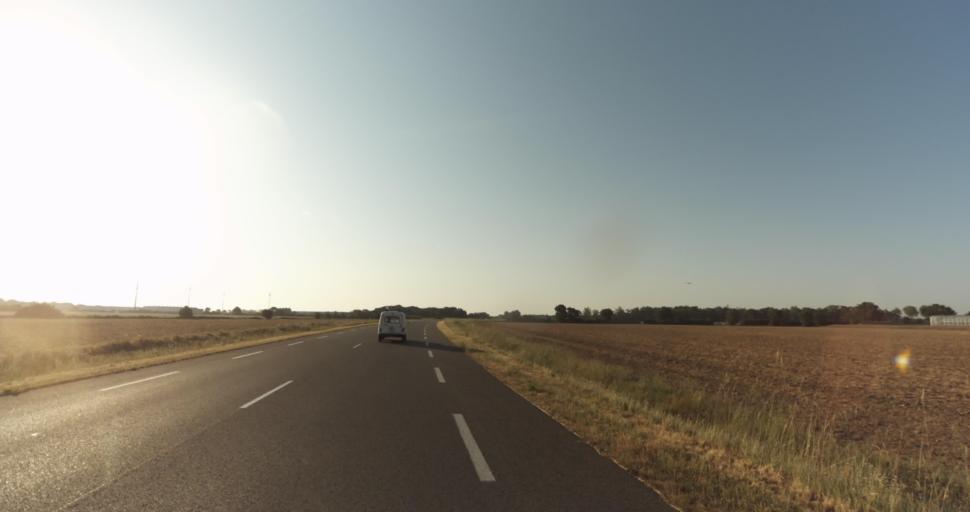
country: FR
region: Midi-Pyrenees
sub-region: Departement de la Haute-Garonne
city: Fontenilles
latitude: 43.5289
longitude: 1.1985
